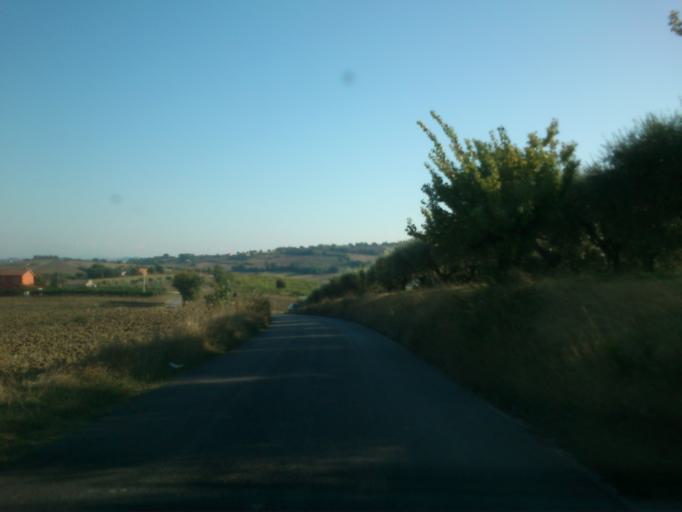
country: IT
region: The Marches
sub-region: Provincia di Pesaro e Urbino
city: Lucrezia
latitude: 43.7874
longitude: 12.9102
